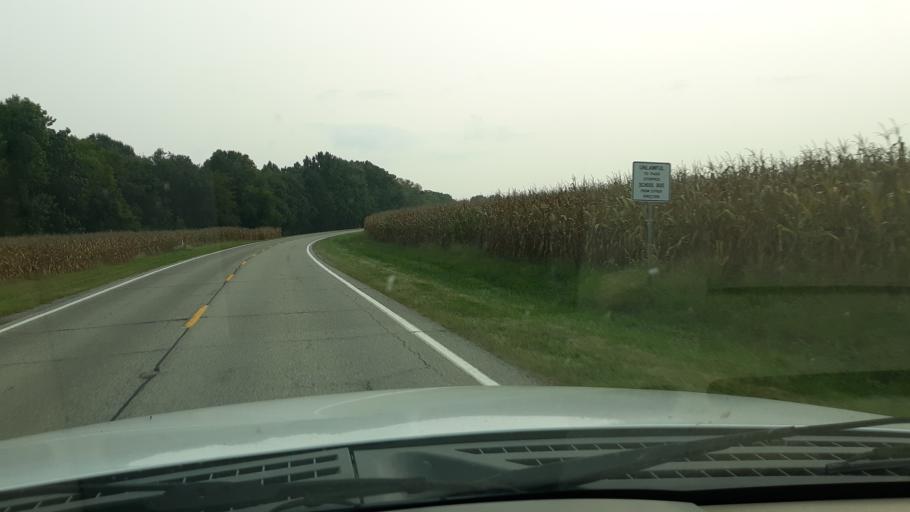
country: US
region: Illinois
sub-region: Edwards County
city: Grayville
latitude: 38.3084
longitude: -87.9429
